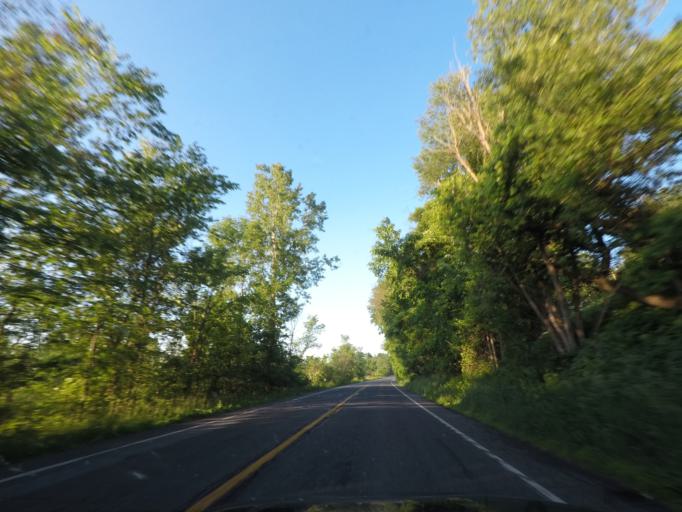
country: US
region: New York
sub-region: Dutchess County
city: Pine Plains
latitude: 41.9865
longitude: -73.5207
